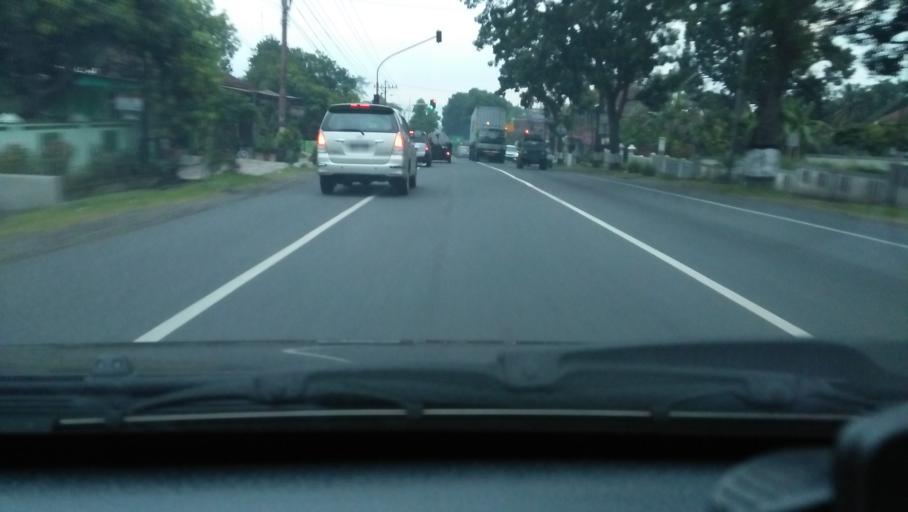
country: ID
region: Central Java
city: Magelang
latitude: -7.4053
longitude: 110.2393
